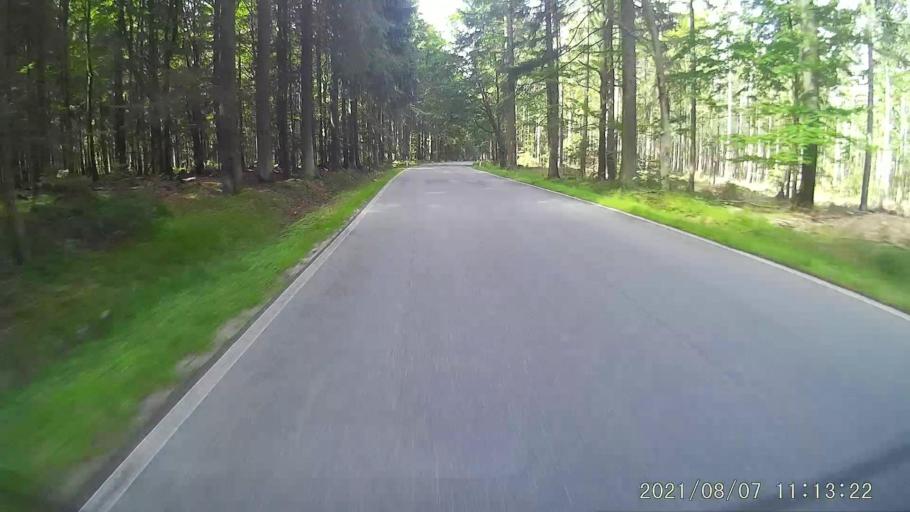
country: PL
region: Lower Silesian Voivodeship
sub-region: Powiat klodzki
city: Bystrzyca Klodzka
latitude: 50.2759
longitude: 16.5223
